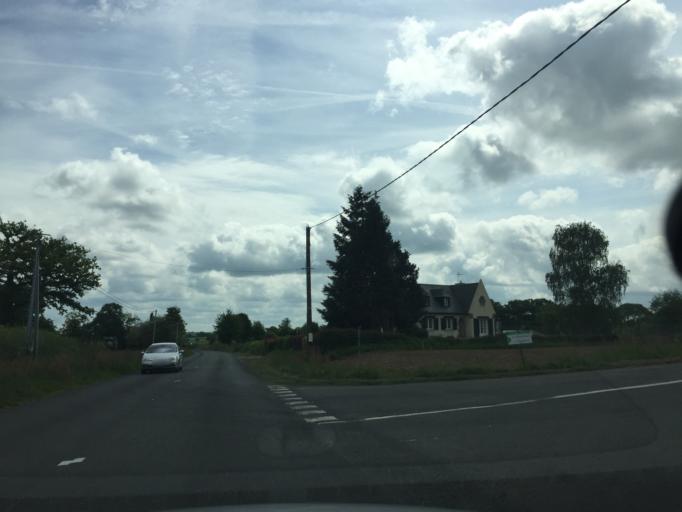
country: FR
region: Brittany
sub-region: Departement des Cotes-d'Armor
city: Quevert
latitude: 48.4754
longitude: -2.0715
